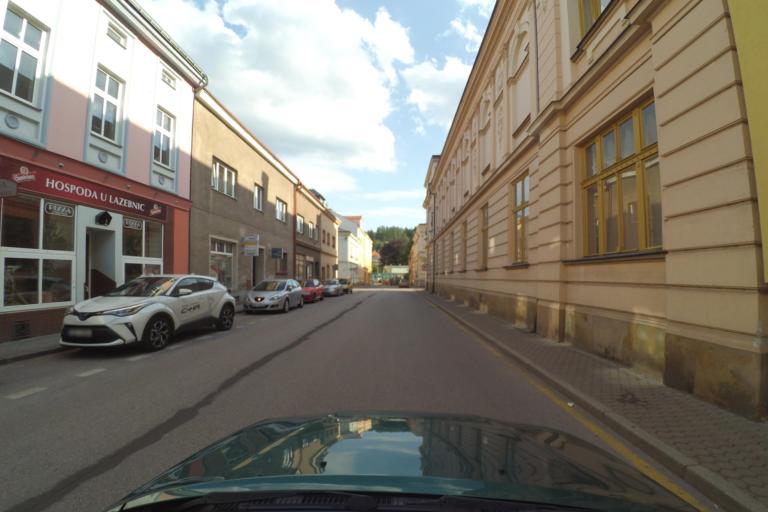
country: CZ
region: Kralovehradecky
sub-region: Okres Trutnov
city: Trutnov
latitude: 50.5645
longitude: 15.9178
